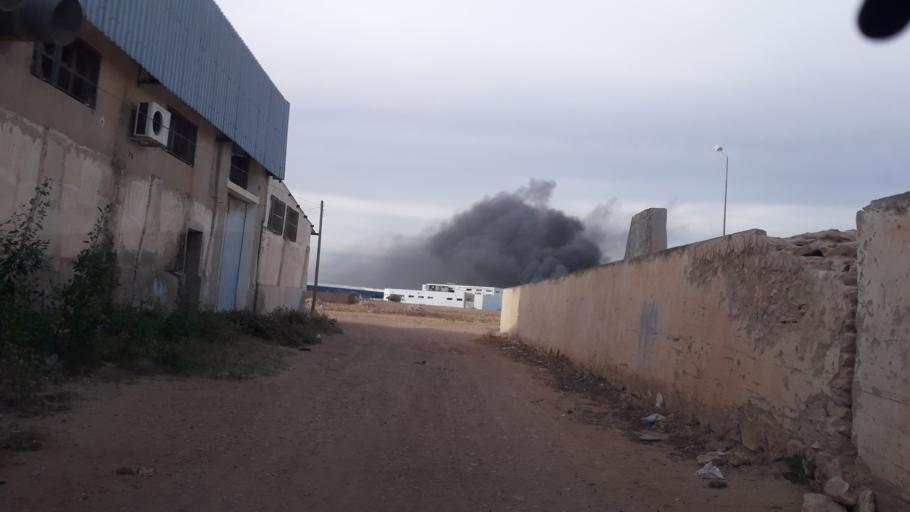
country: TN
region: Safaqis
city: Al Qarmadah
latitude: 34.8877
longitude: 10.7589
